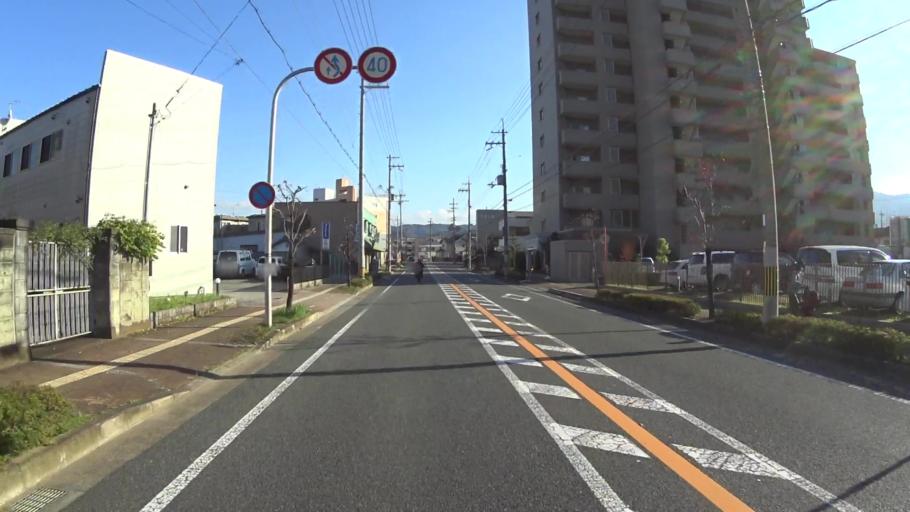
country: JP
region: Kyoto
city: Fukuchiyama
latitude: 35.3030
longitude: 135.1122
